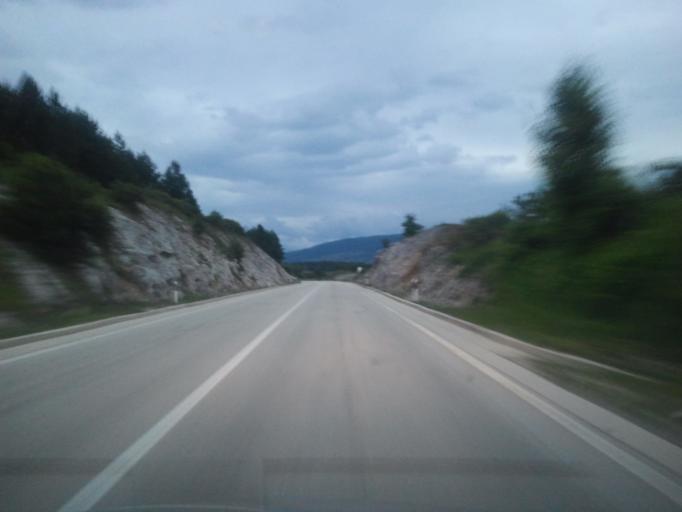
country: HR
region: Zadarska
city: Gracac
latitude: 44.3676
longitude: 15.8728
